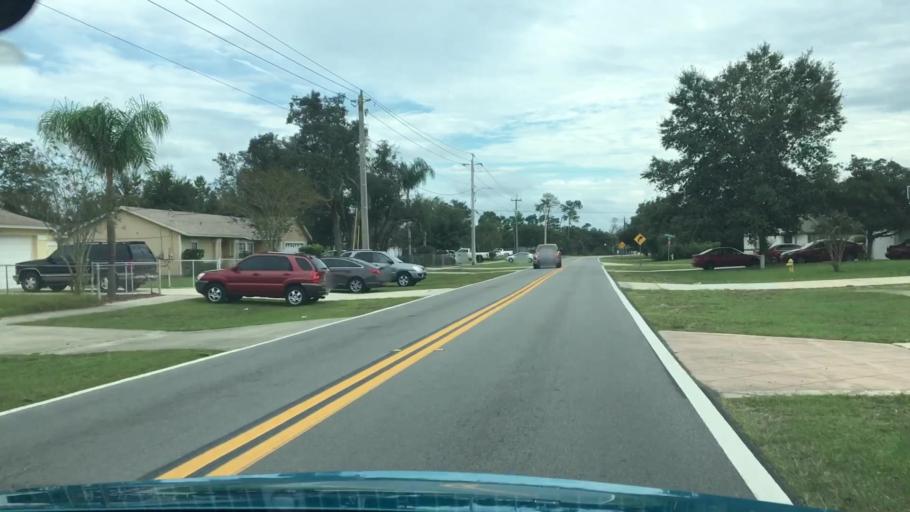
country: US
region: Florida
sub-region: Volusia County
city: Lake Helen
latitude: 28.9432
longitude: -81.1830
